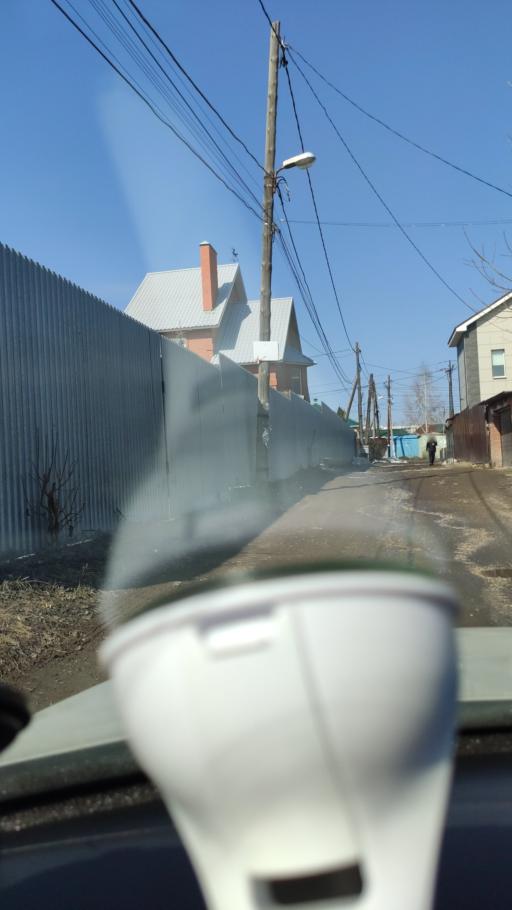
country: RU
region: Samara
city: Petra-Dubrava
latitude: 53.2926
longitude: 50.2789
